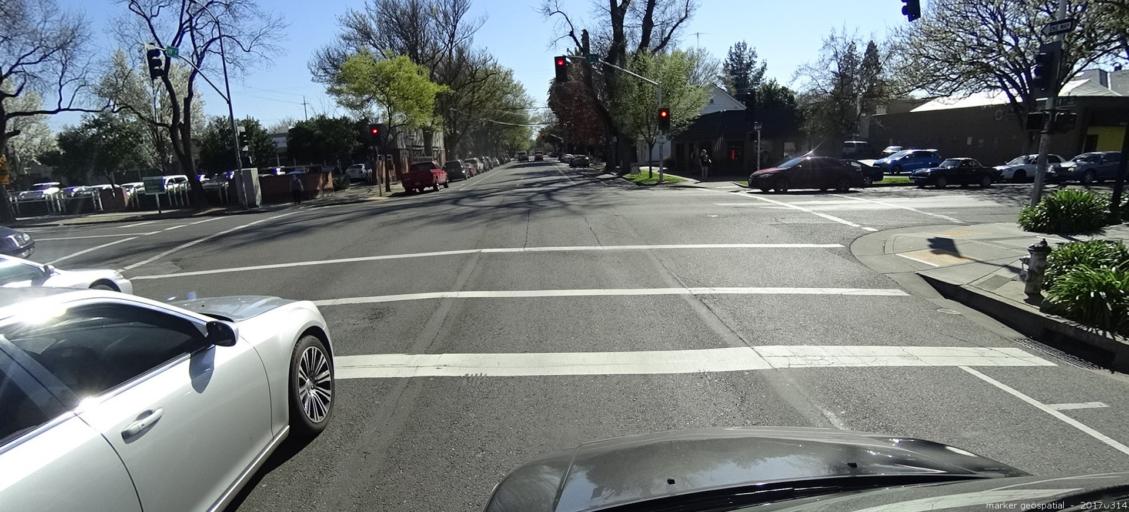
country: US
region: California
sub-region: Sacramento County
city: Sacramento
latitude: 38.5673
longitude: -121.4855
